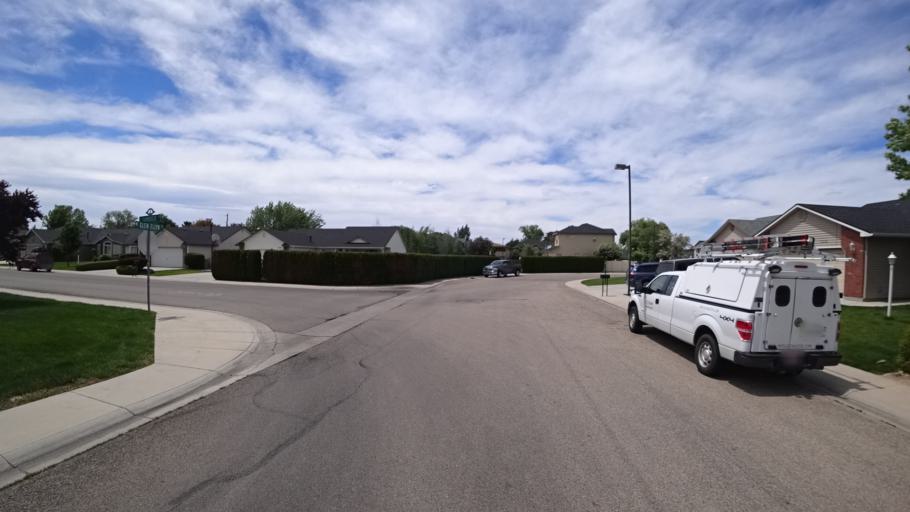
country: US
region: Idaho
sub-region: Ada County
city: Meridian
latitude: 43.6264
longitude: -116.3237
